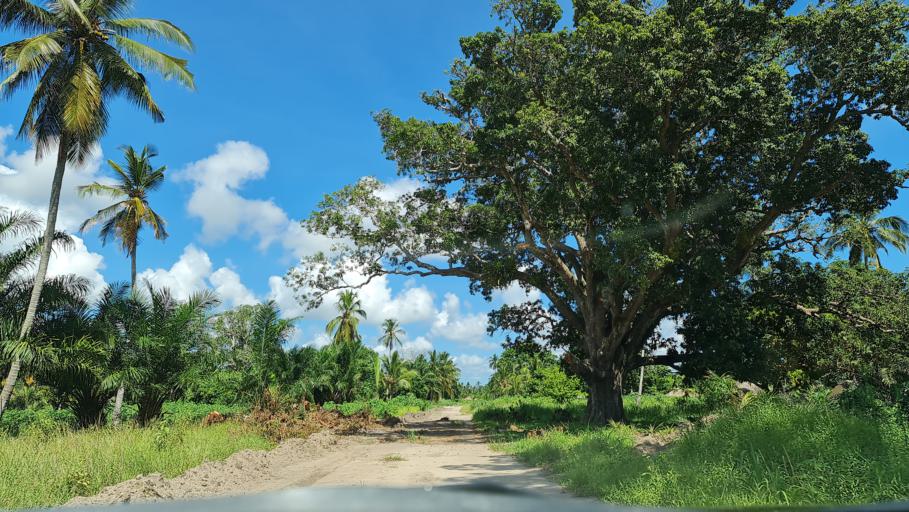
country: MZ
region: Zambezia
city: Quelimane
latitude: -17.3828
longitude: 37.5168
